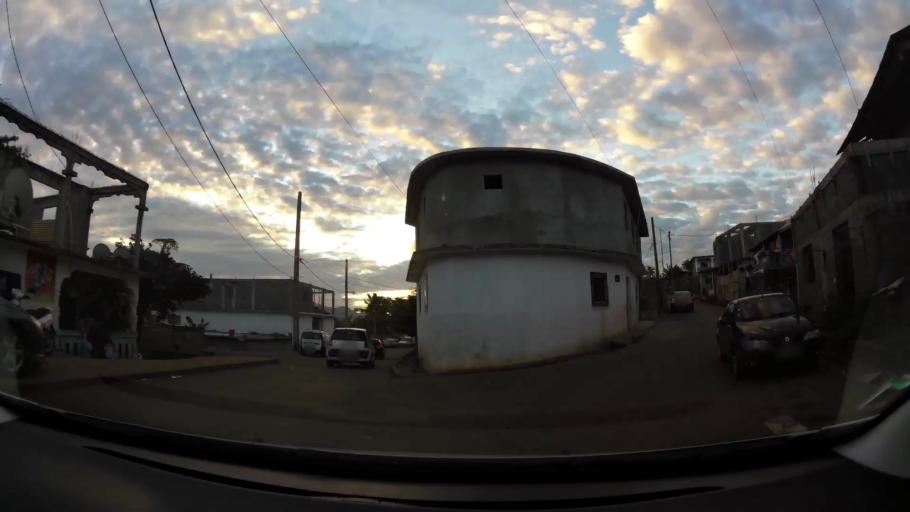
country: YT
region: Koungou
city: Koungou
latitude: -12.7359
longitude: 45.1640
